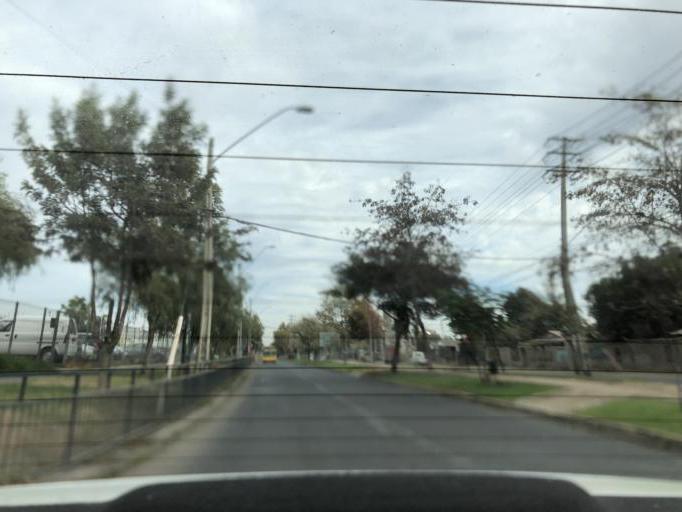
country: CL
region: Santiago Metropolitan
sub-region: Provincia de Cordillera
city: Puente Alto
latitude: -33.6100
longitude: -70.5510
